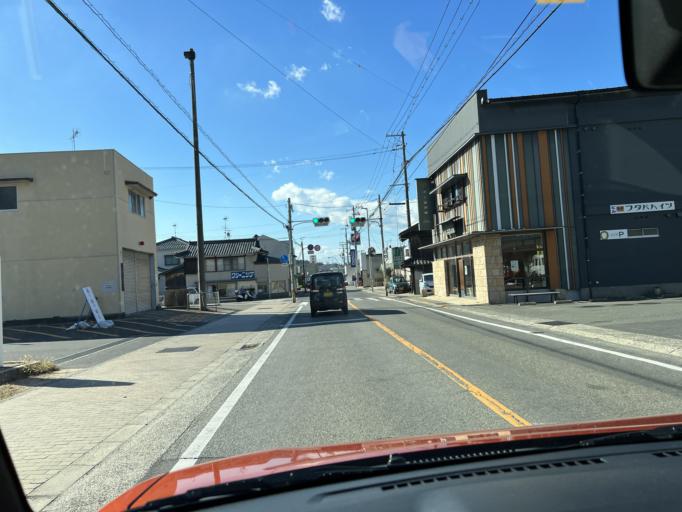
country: JP
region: Kagawa
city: Tonosho
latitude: 34.4830
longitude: 134.2335
